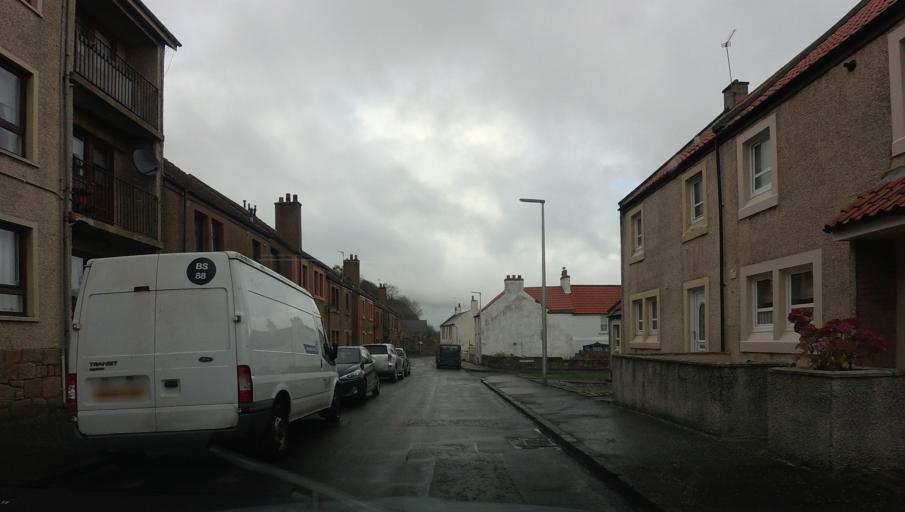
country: GB
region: Scotland
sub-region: Fife
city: East Wemyss
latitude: 56.1407
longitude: -3.0843
